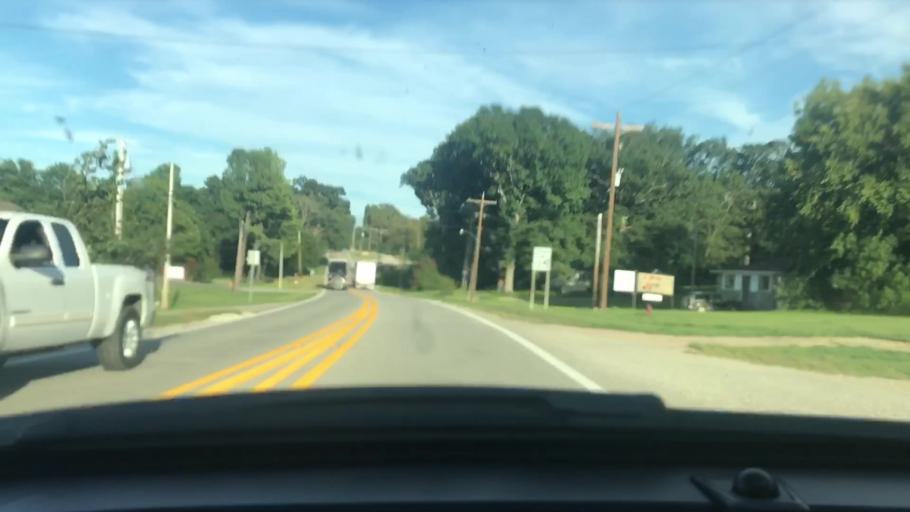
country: US
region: Arkansas
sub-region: Randolph County
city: Pocahontas
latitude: 36.2039
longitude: -91.1903
